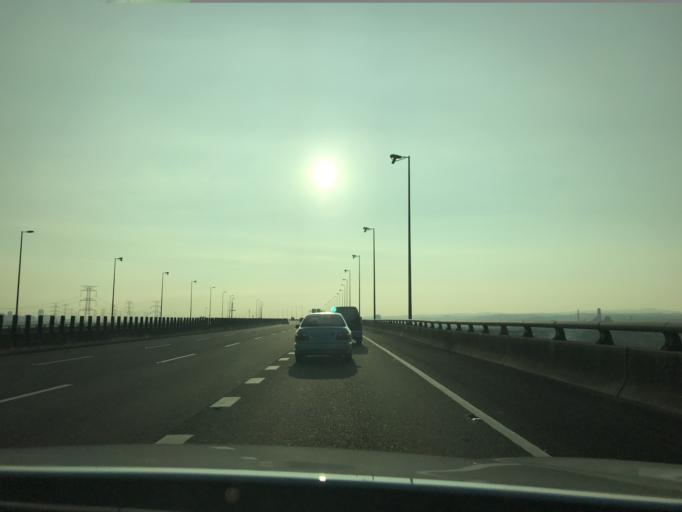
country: TW
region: Taiwan
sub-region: Changhua
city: Chang-hua
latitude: 24.1096
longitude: 120.5480
